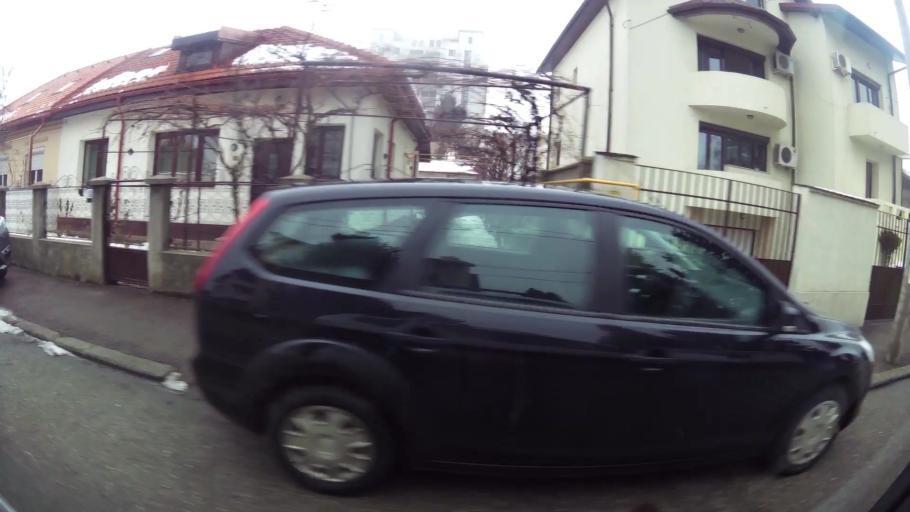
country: RO
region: Ilfov
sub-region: Comuna Chiajna
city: Rosu
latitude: 44.4438
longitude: 26.0249
